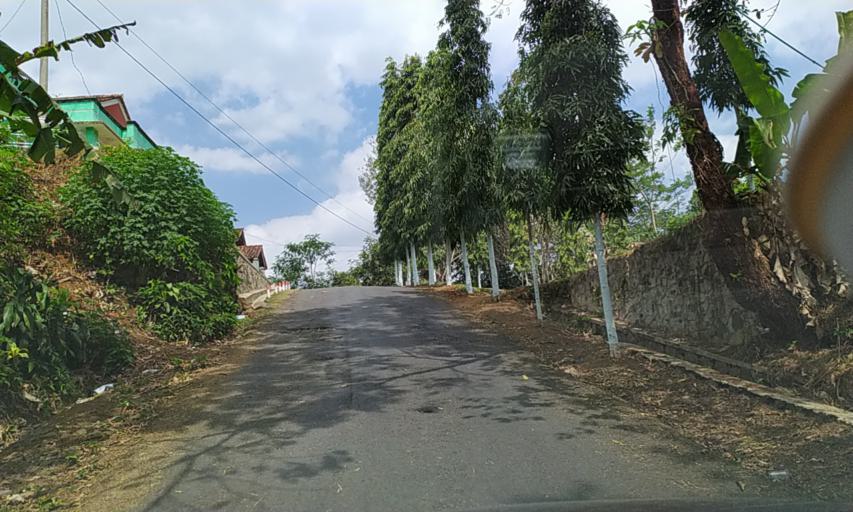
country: ID
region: Central Java
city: Kubang
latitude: -7.2706
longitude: 108.6447
